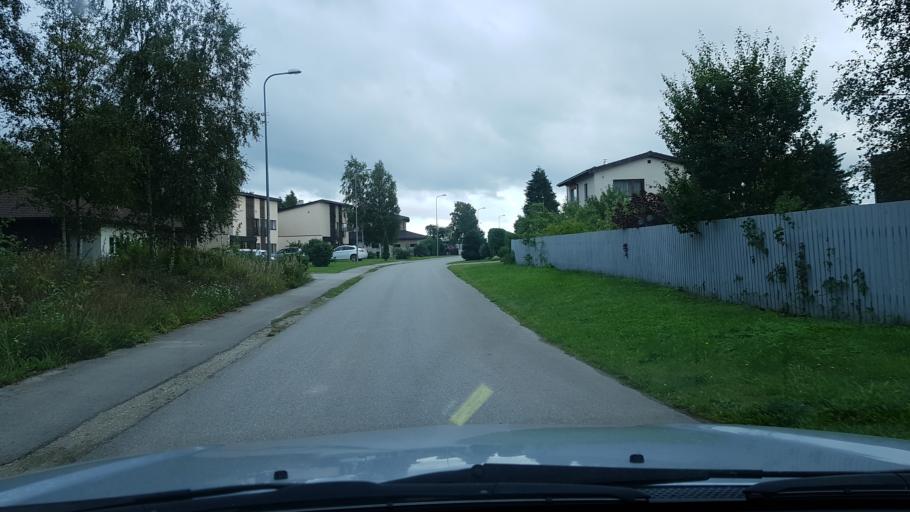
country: EE
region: Harju
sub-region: Rae vald
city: Jueri
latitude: 59.3969
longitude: 24.8403
